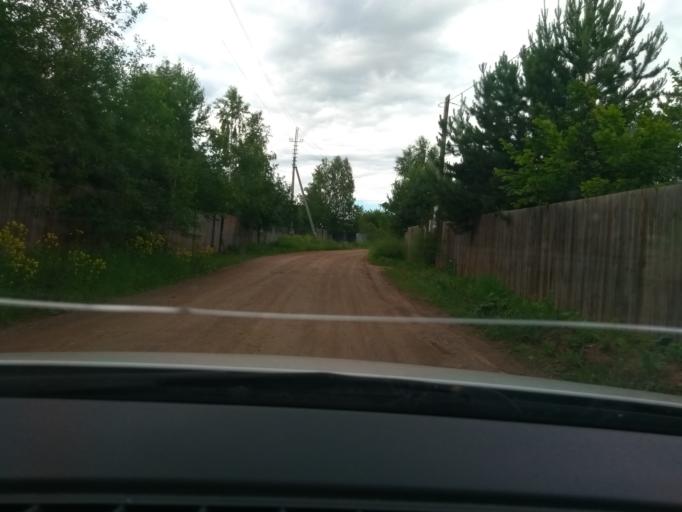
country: RU
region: Perm
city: Sylva
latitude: 57.8431
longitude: 56.7953
